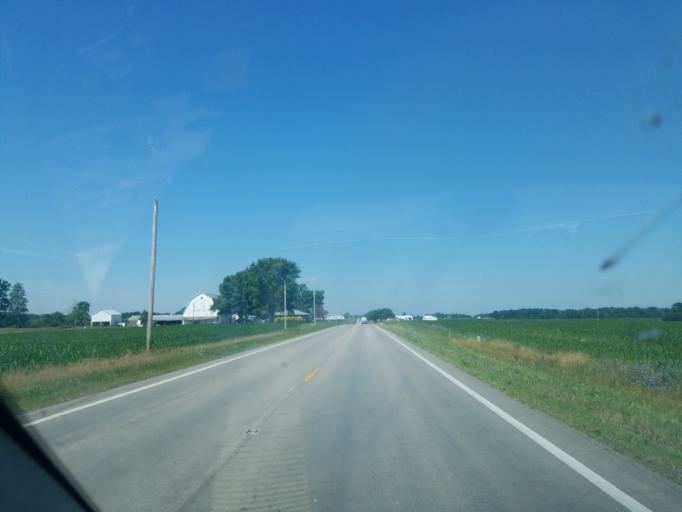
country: US
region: Ohio
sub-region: Shelby County
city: Botkins
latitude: 40.4388
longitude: -84.2320
